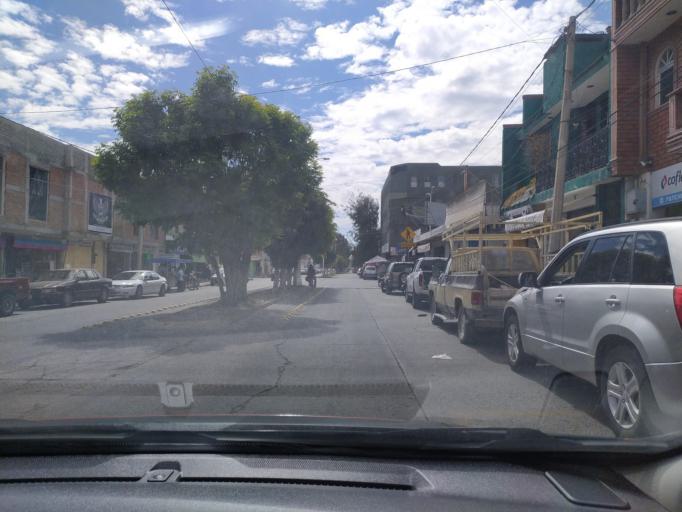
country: LA
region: Oudomxai
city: Muang La
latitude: 21.0129
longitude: 101.8575
